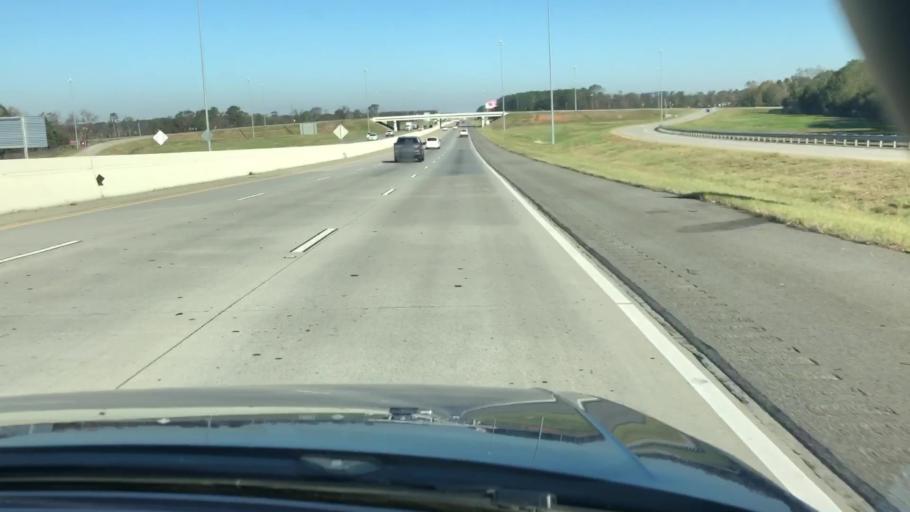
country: US
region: Georgia
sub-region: Crisp County
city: Cordele
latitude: 31.9707
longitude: -83.7531
